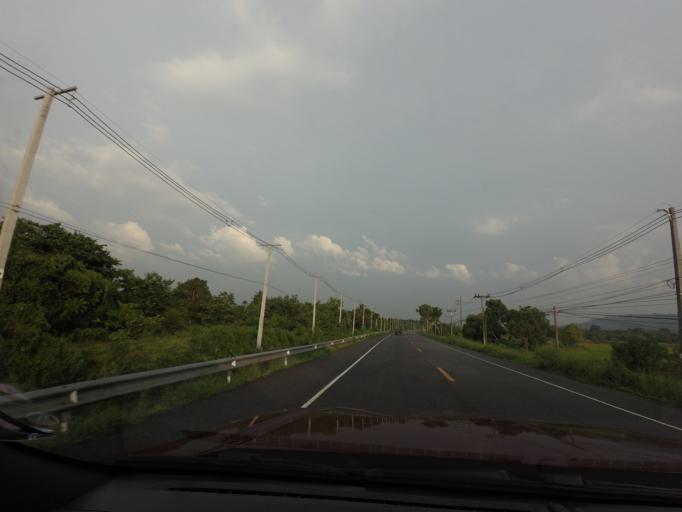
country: TH
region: Pattani
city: Mae Lan
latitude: 6.6424
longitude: 101.1834
